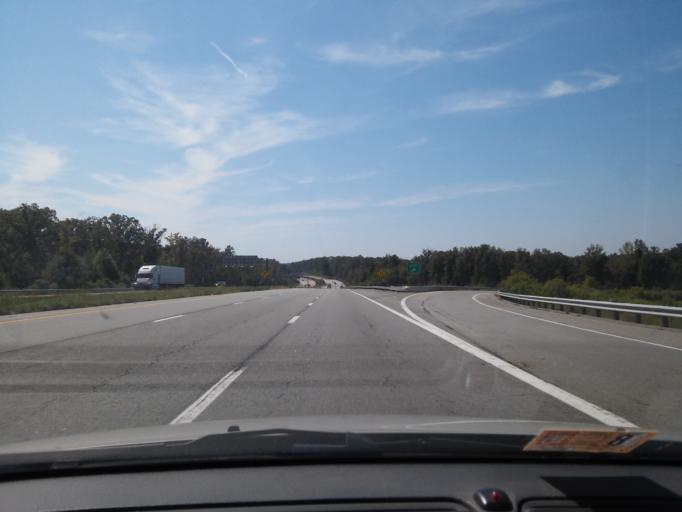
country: US
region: Virginia
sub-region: Henrico County
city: Short Pump
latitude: 37.6632
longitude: -77.6576
